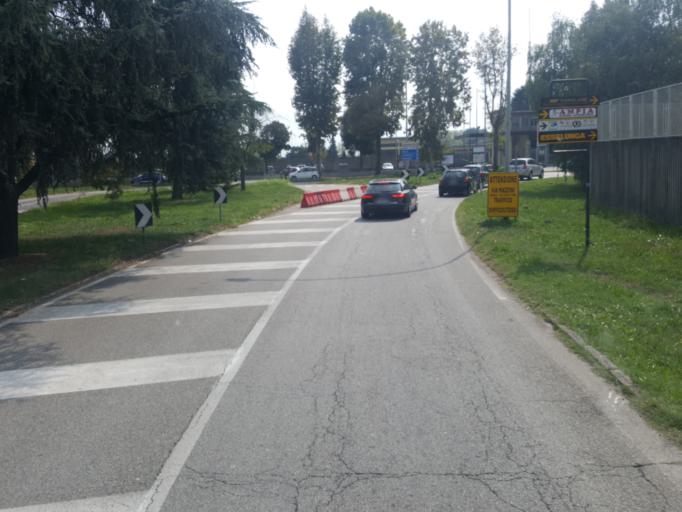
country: IT
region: Lombardy
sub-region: Citta metropolitana di Milano
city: Abbiategrasso
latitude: 45.4005
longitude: 8.9323
